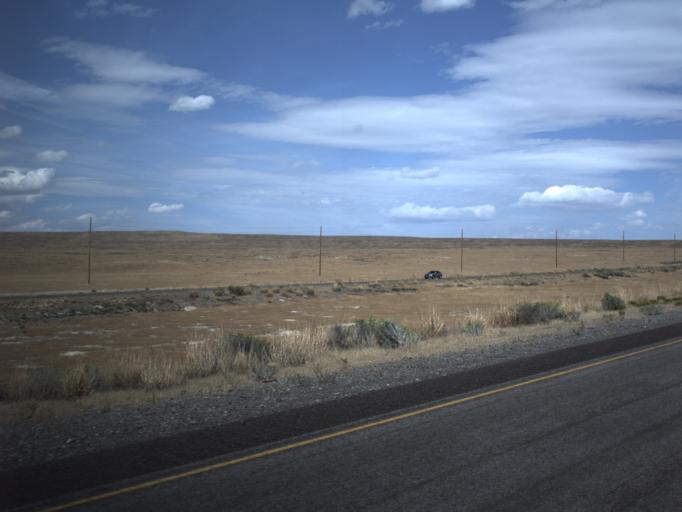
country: US
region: Utah
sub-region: Tooele County
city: Grantsville
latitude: 40.7539
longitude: -113.0321
